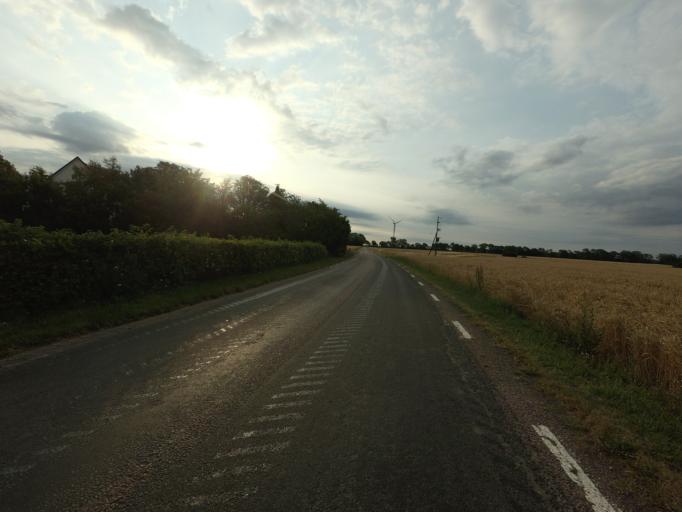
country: SE
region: Skane
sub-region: Helsingborg
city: Odakra
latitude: 56.1508
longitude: 12.6468
